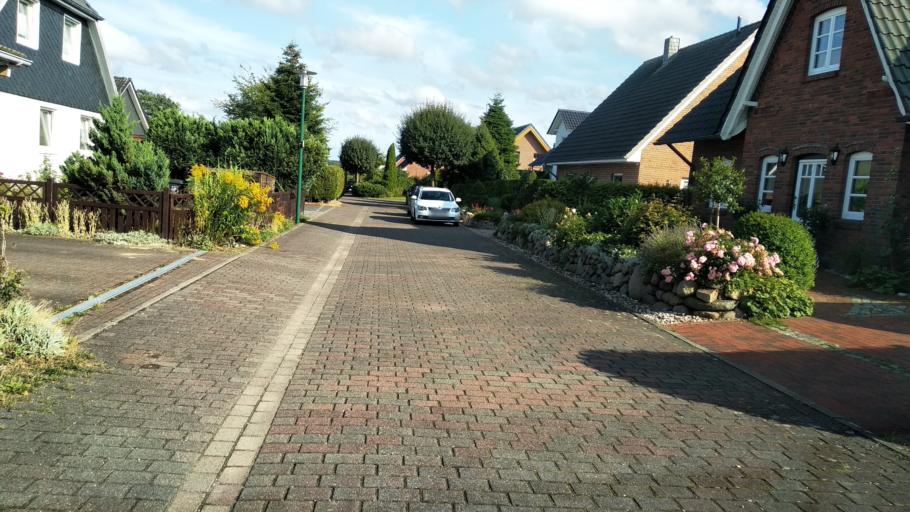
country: DE
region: Schleswig-Holstein
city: Busdorf
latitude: 54.4866
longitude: 9.5408
